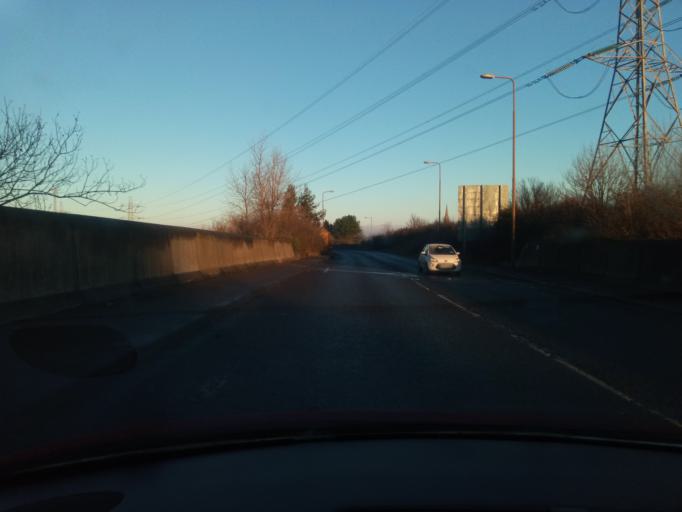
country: GB
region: Scotland
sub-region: West Lothian
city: Seafield
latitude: 55.9456
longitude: -3.1037
